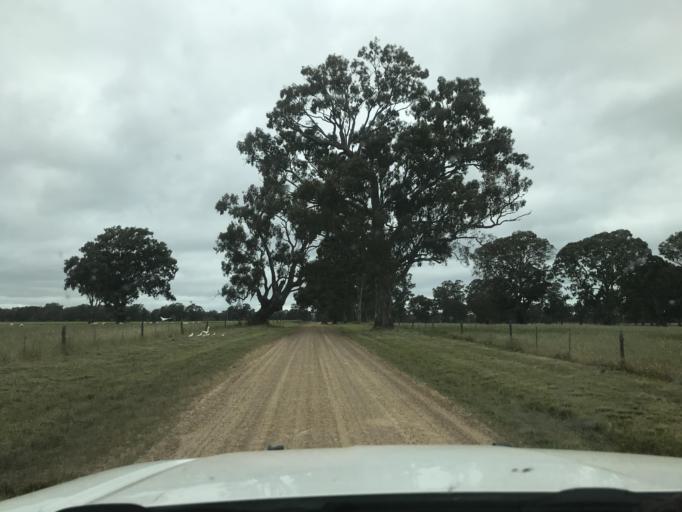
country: AU
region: South Australia
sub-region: Wattle Range
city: Penola
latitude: -37.2739
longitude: 140.9829
